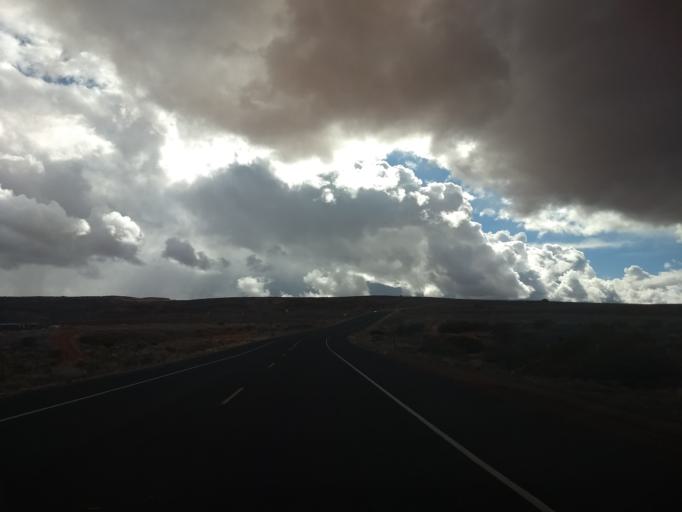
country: US
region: Utah
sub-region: Washington County
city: Washington
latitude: 37.1103
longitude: -113.3937
